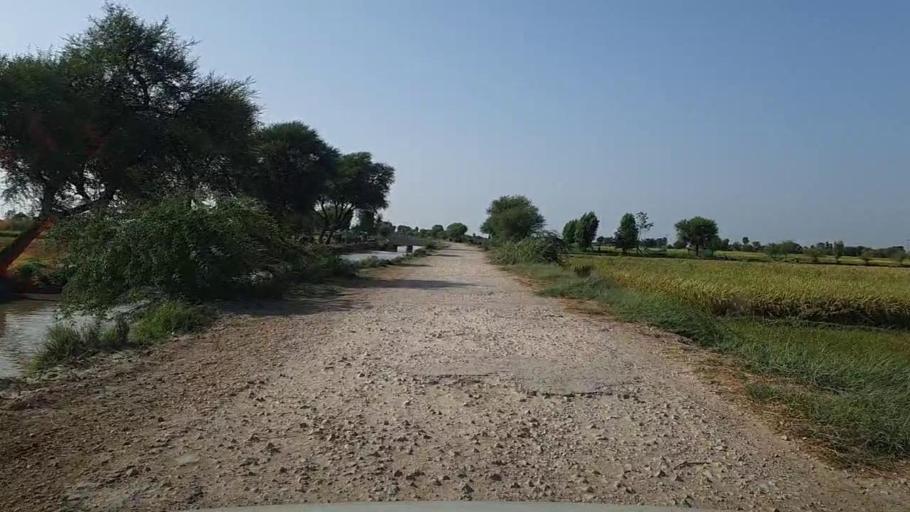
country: PK
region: Sindh
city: Kario
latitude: 24.8011
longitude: 68.5532
